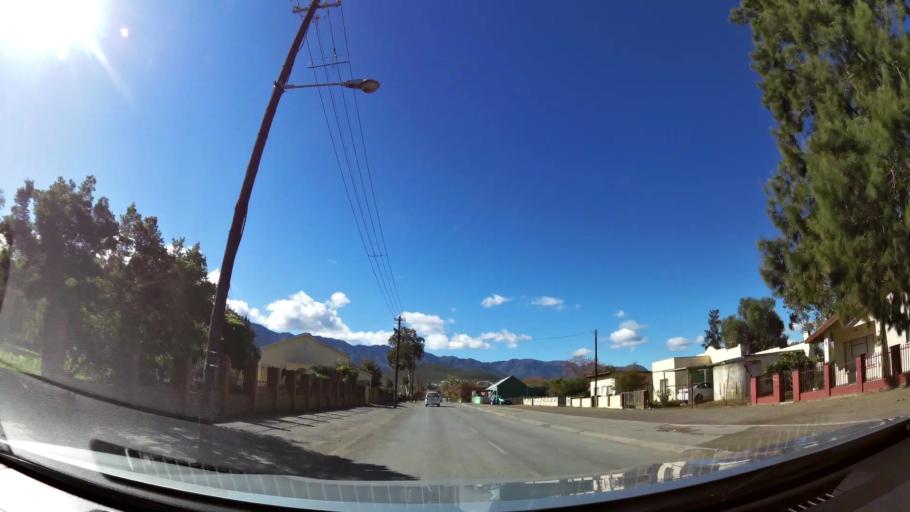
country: ZA
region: Western Cape
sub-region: Cape Winelands District Municipality
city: Ashton
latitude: -33.7950
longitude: 19.8853
